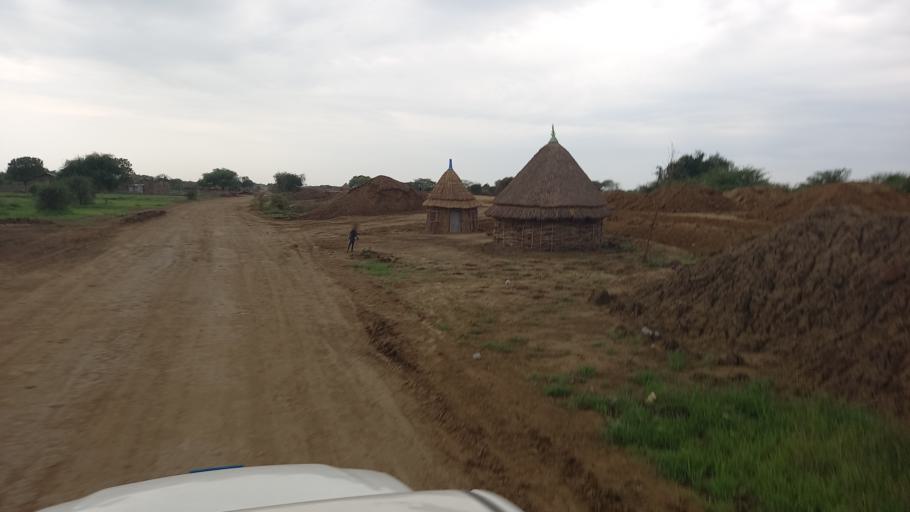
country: ET
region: Gambela
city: Gambela
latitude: 8.3348
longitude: 33.9430
